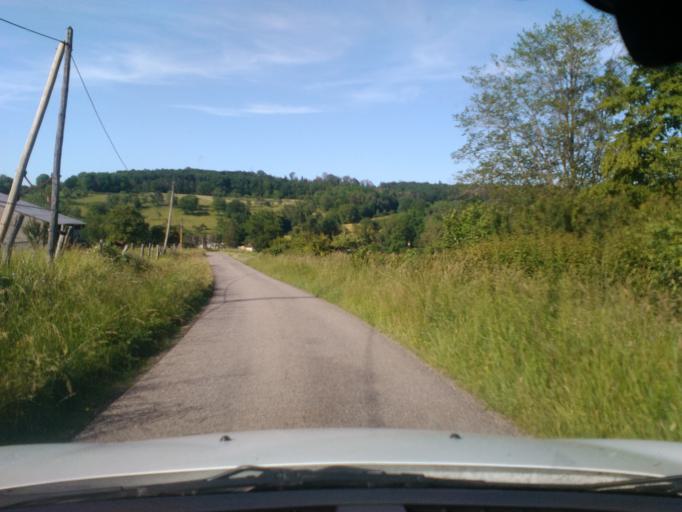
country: FR
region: Lorraine
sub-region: Departement des Vosges
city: Mirecourt
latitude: 48.2628
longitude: 6.2280
